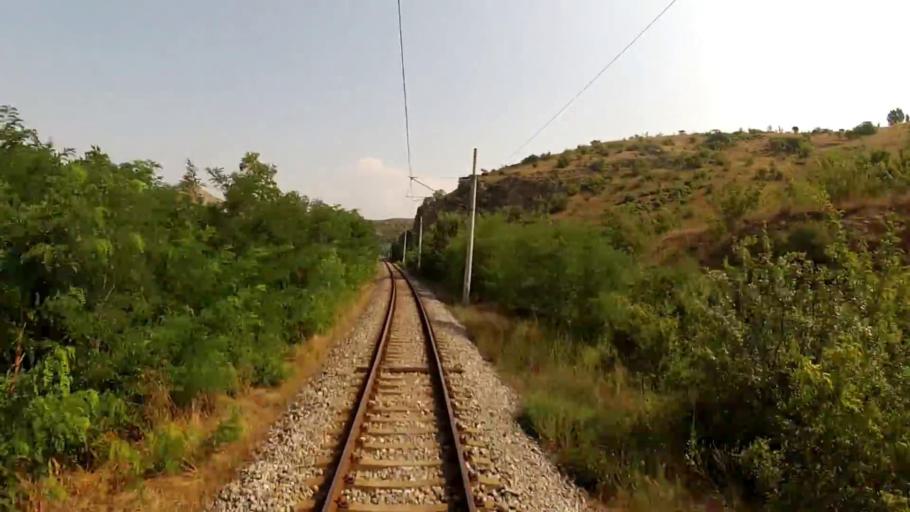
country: BG
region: Blagoevgrad
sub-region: Obshtina Sandanski
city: Sandanski
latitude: 41.4847
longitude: 23.2744
